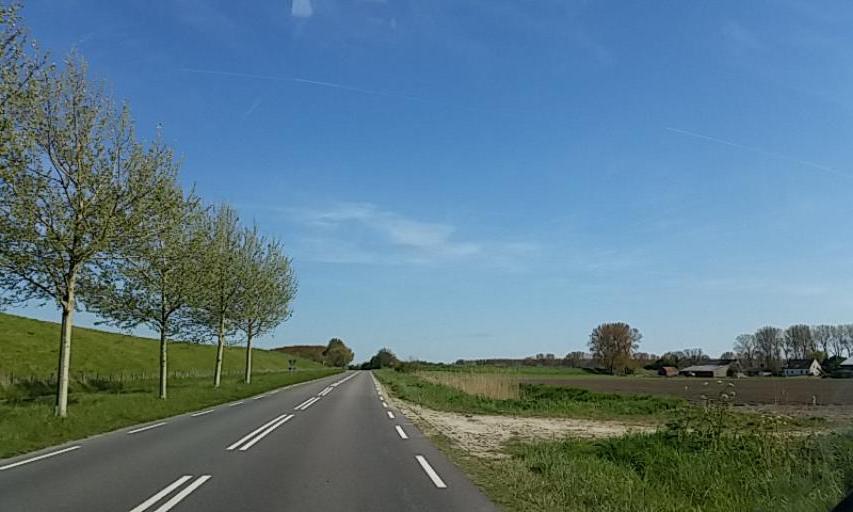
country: NL
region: Zeeland
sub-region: Gemeente Vlissingen
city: Vlissingen
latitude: 51.3893
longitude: 3.5813
